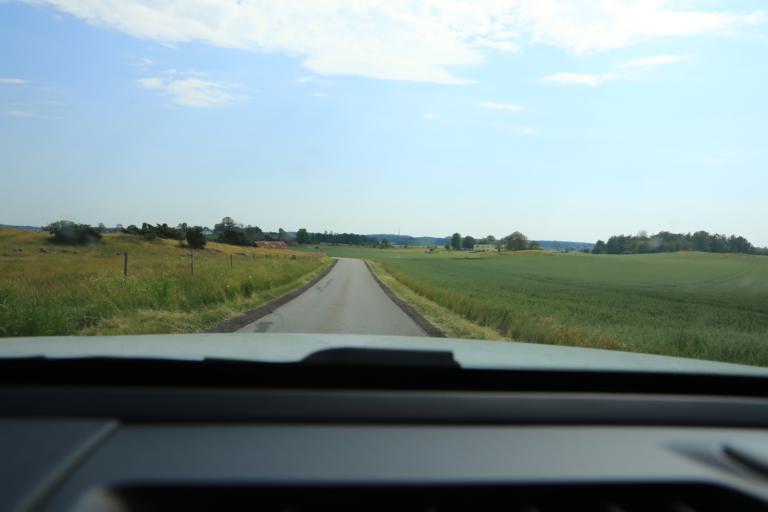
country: SE
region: Halland
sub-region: Varbergs Kommun
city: Varberg
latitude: 57.1366
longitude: 12.3276
